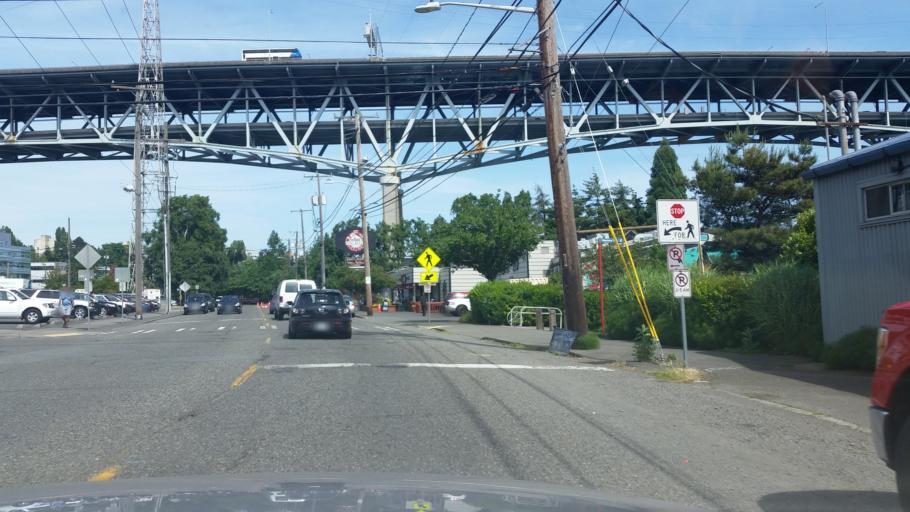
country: US
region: Washington
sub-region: King County
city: Seattle
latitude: 47.6538
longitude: -122.3249
